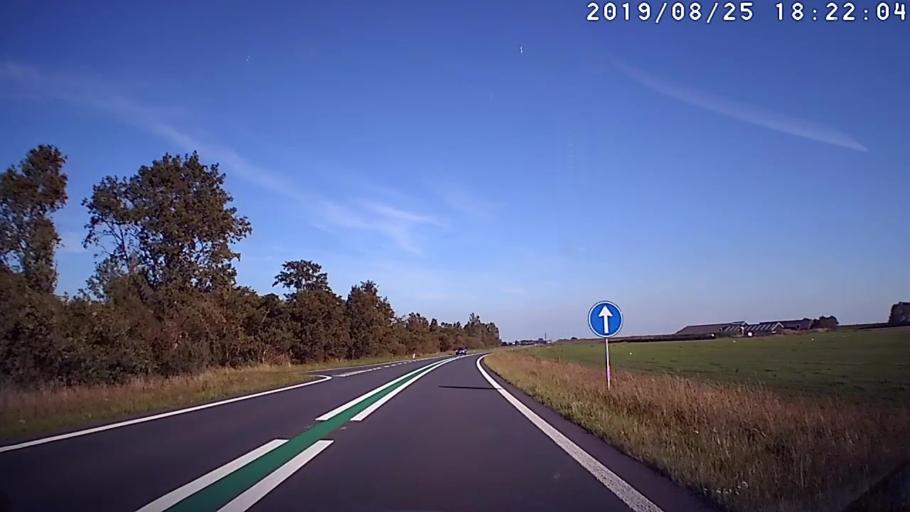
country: NL
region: Friesland
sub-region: Gemeente Lemsterland
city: Lemmer
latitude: 52.8686
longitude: 5.6436
